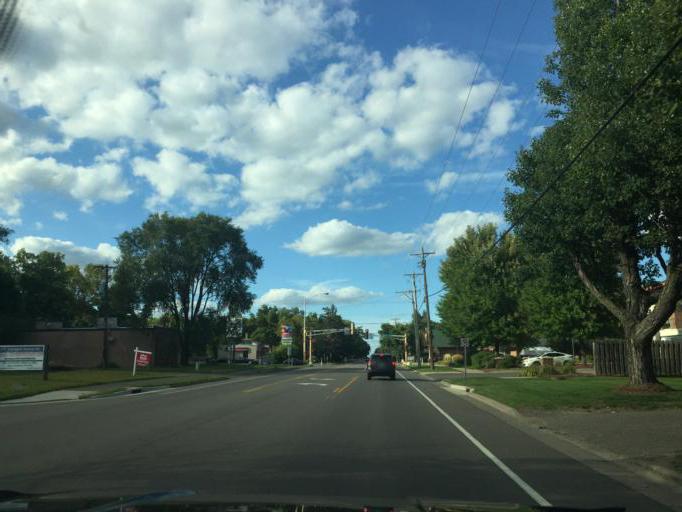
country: US
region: Minnesota
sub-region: Ramsey County
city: Roseville
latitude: 44.9982
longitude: -93.1463
